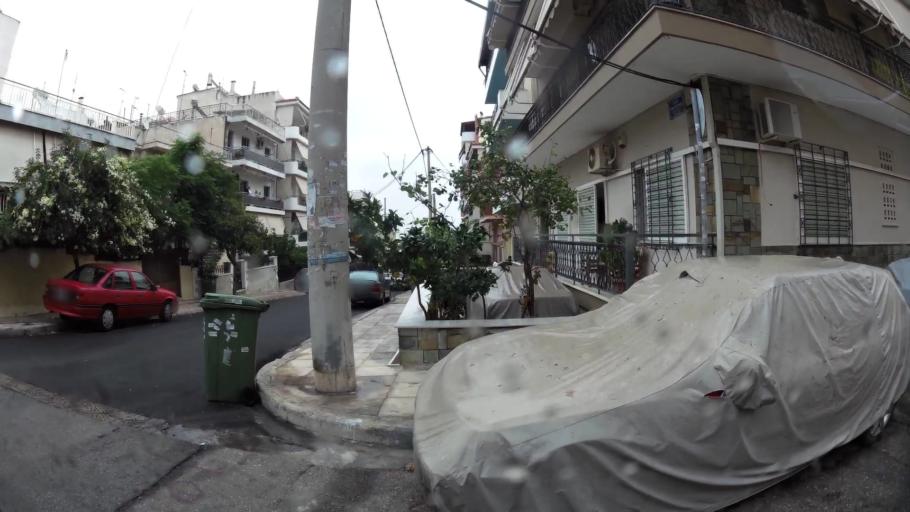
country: GR
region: Attica
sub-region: Nomos Piraios
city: Korydallos
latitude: 37.9853
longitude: 23.6396
